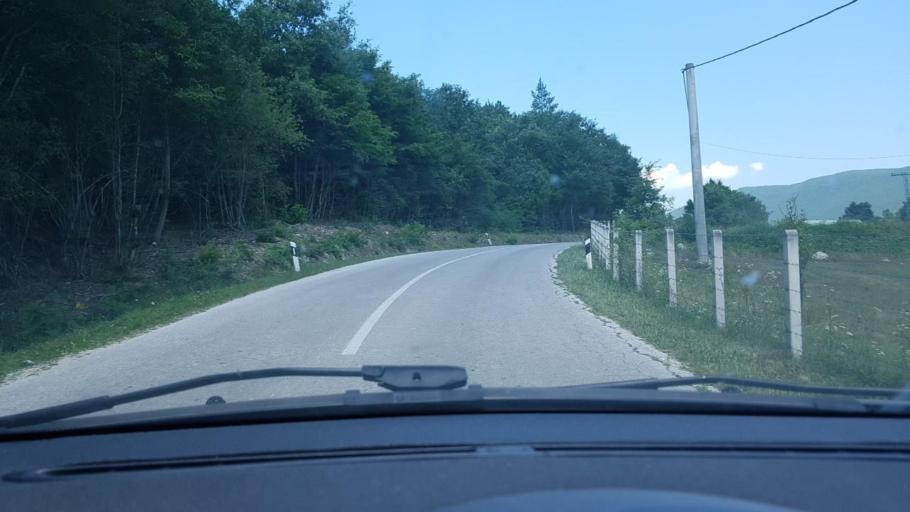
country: BA
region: Federation of Bosnia and Herzegovina
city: Orasac
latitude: 44.6059
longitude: 16.0698
